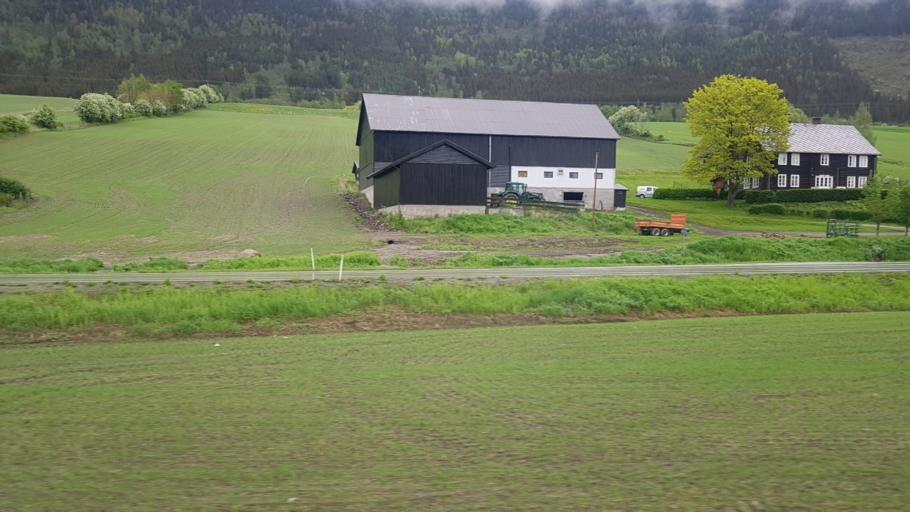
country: NO
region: Oppland
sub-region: Nord-Fron
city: Vinstra
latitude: 61.6185
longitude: 9.7131
